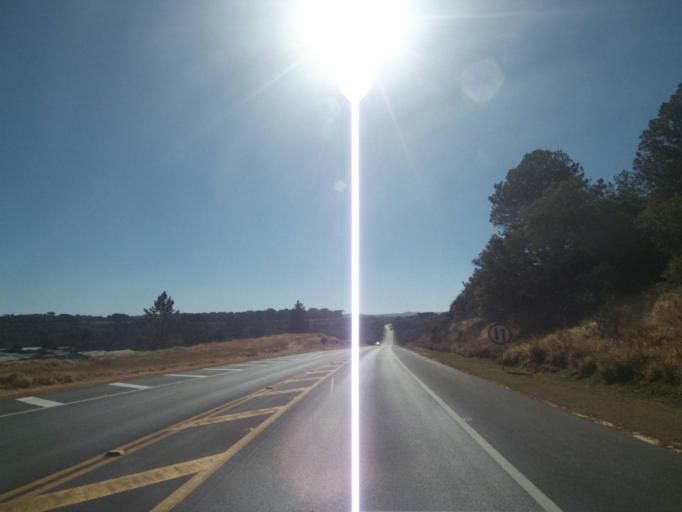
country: BR
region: Parana
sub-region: Tibagi
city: Tibagi
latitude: -24.7430
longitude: -50.5377
